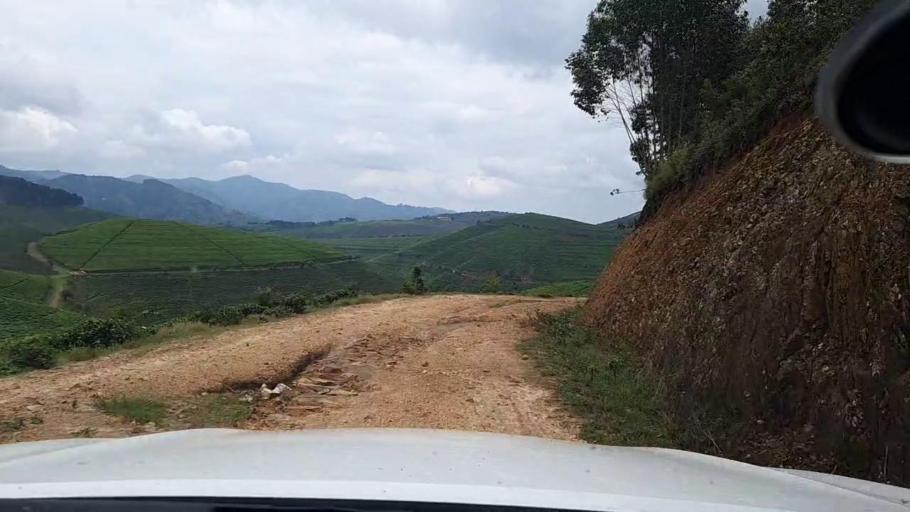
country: RW
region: Western Province
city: Kibuye
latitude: -2.1576
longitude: 29.4530
